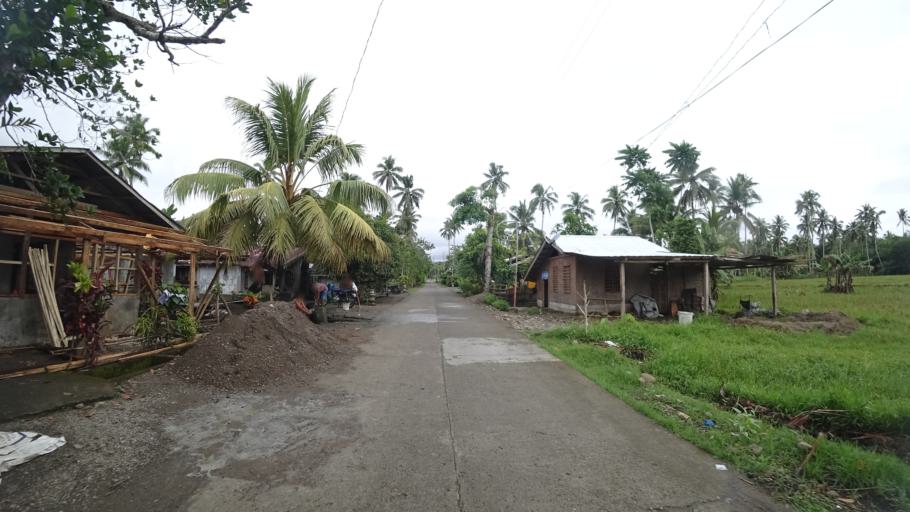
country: PH
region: Eastern Visayas
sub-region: Province of Leyte
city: Bugho
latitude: 10.8235
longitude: 124.9272
